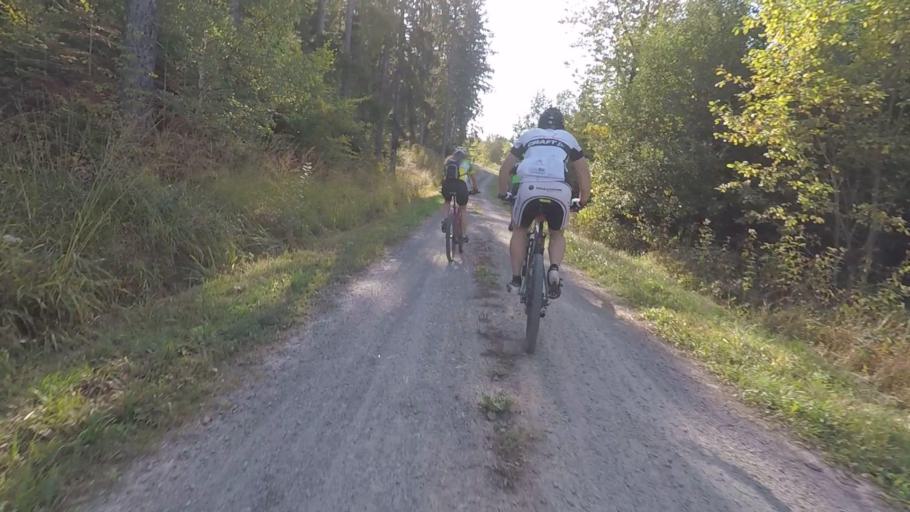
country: DE
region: Baden-Wuerttemberg
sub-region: Regierungsbezirk Stuttgart
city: Wustenrot
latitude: 49.0587
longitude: 9.4674
